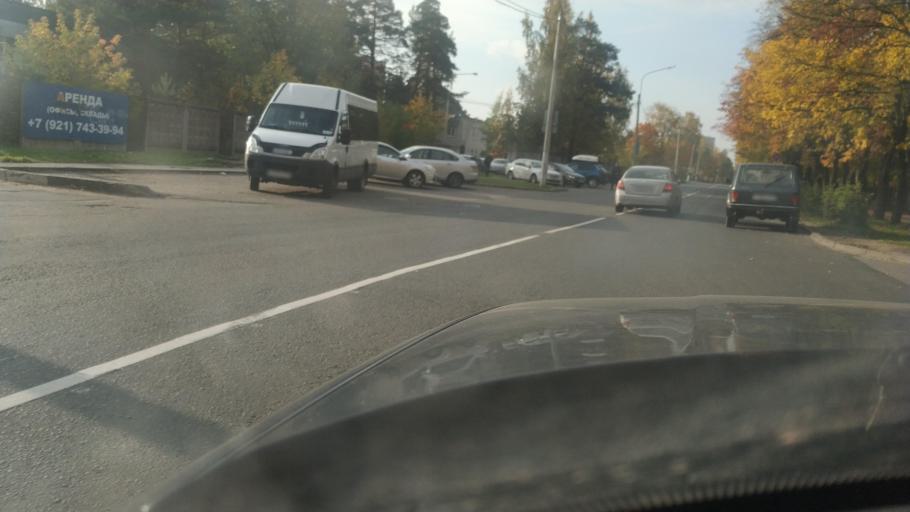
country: RU
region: Leningrad
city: Sosnovyy Bor
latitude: 59.8962
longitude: 29.0993
